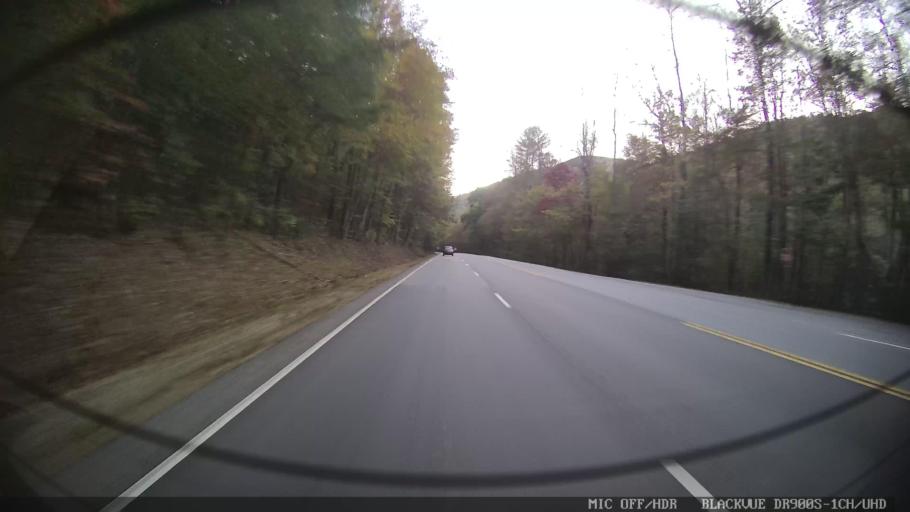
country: US
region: Georgia
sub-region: Union County
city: Blairsville
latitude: 34.7058
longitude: -83.9150
